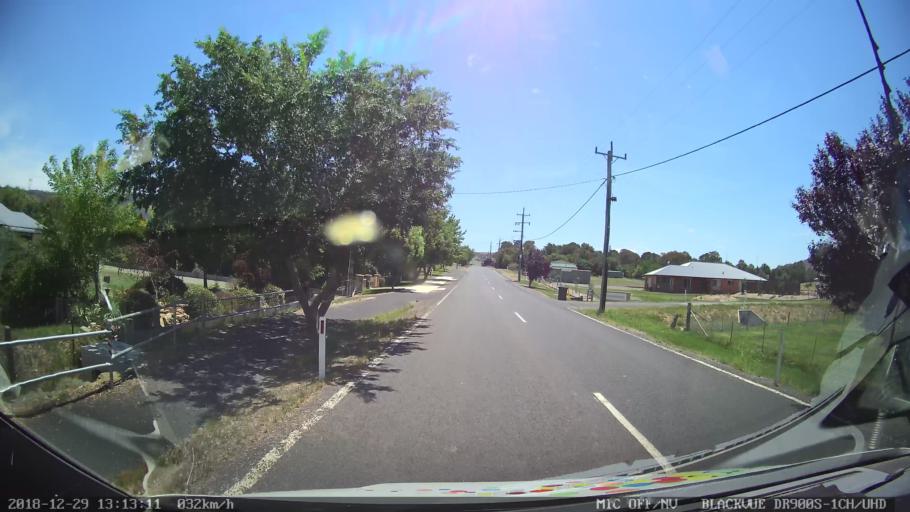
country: AU
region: Australian Capital Territory
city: Macarthur
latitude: -35.7081
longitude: 149.1640
